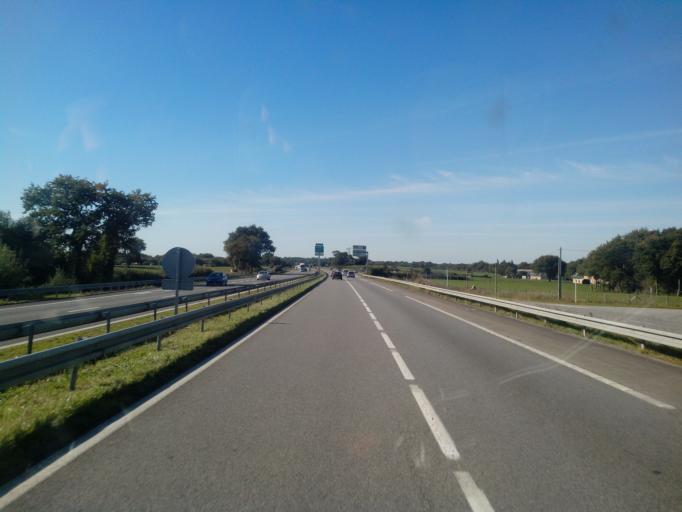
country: FR
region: Brittany
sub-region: Departement du Morbihan
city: Ambon
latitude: 47.5870
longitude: -2.5446
